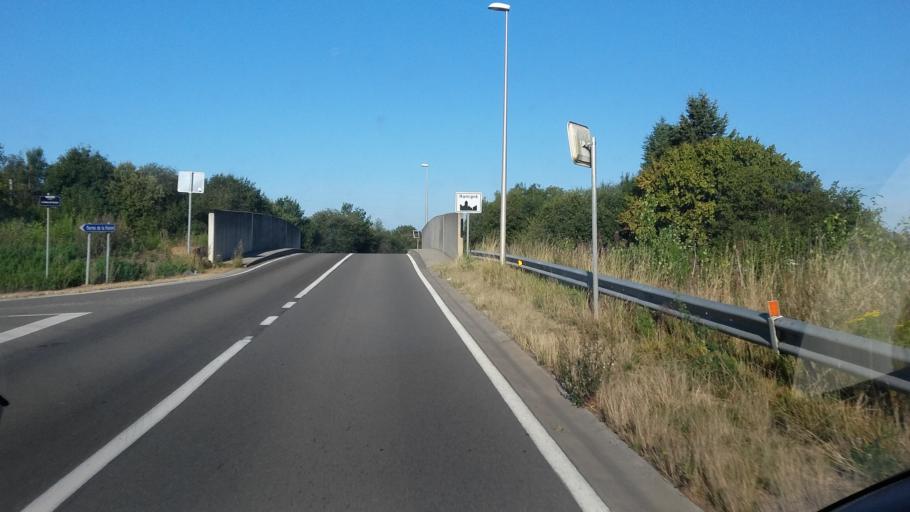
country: BE
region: Wallonia
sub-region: Province du Luxembourg
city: Neufchateau
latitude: 49.8363
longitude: 5.4641
